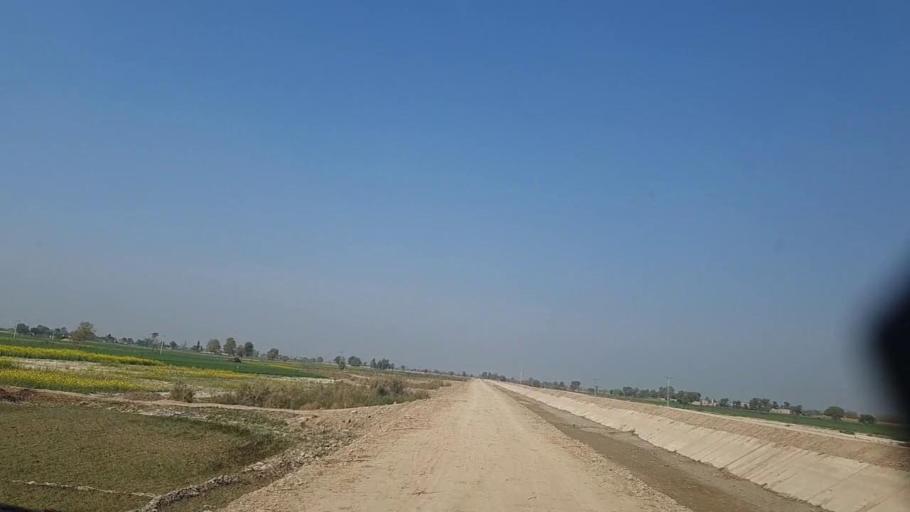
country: PK
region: Sindh
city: Sakrand
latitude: 26.1556
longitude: 68.3288
